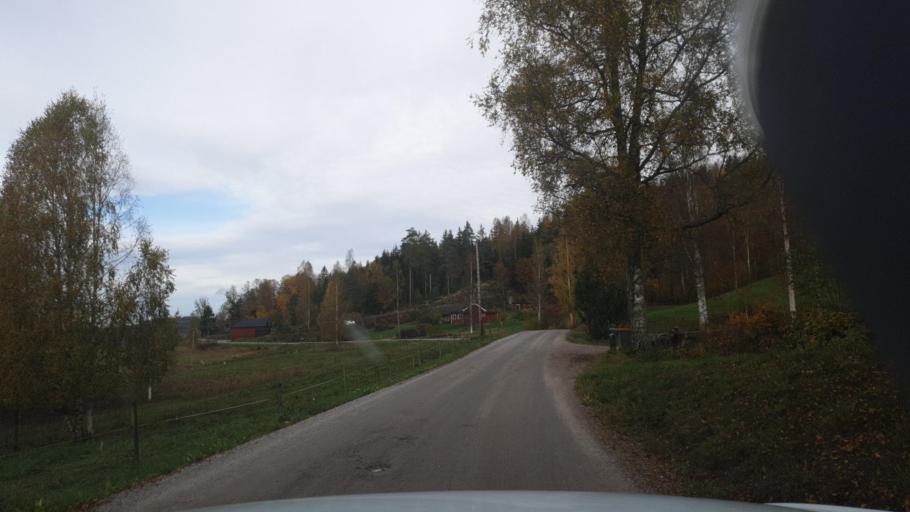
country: SE
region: Vaermland
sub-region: Arvika Kommun
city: Arvika
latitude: 59.7267
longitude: 12.8355
